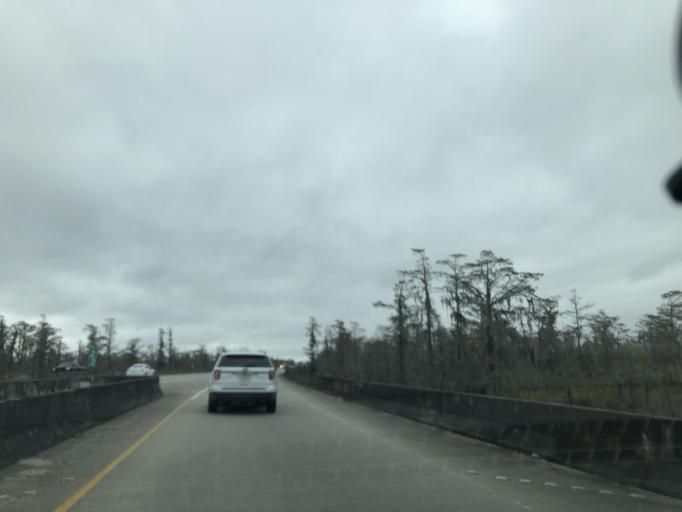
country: US
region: Louisiana
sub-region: Saint Charles Parish
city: Ama
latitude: 29.9799
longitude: -90.3129
